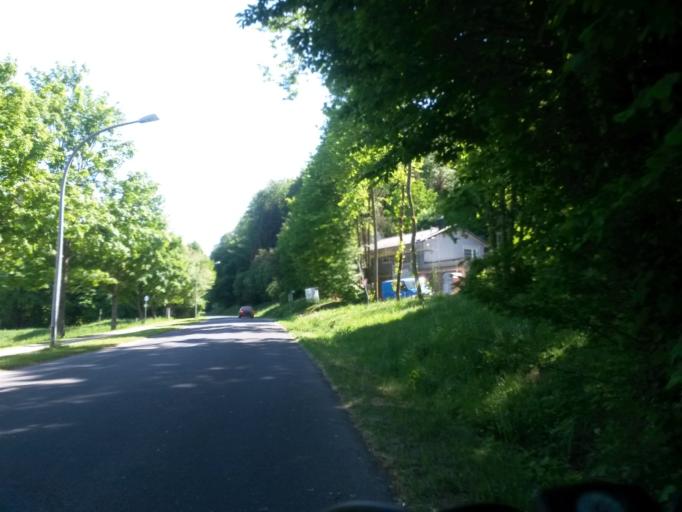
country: DE
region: Bavaria
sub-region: Regierungsbezirk Unterfranken
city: Bad Kissingen
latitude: 50.2069
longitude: 10.0677
